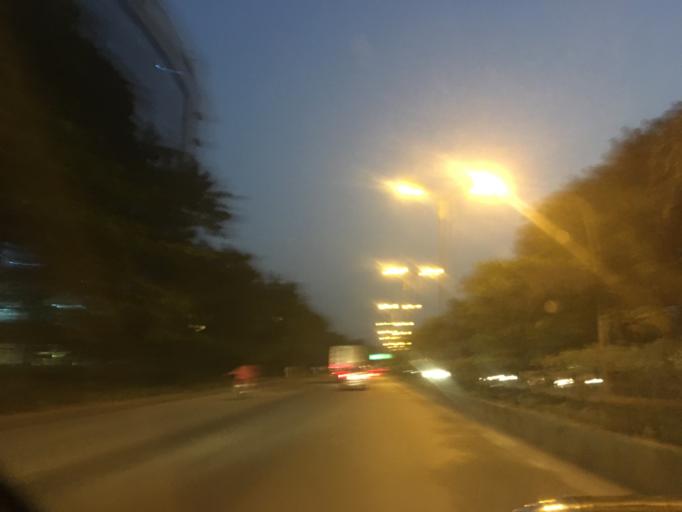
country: IN
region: Maharashtra
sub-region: Thane
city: Airoli
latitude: 19.1542
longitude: 73.0005
